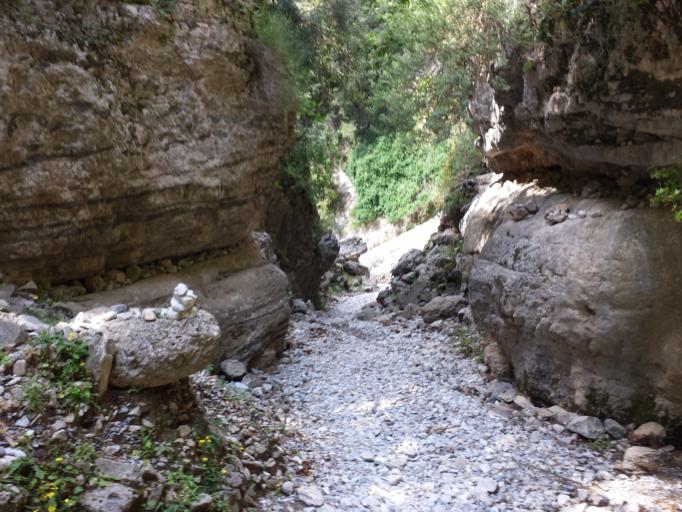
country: GR
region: Crete
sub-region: Nomos Chanias
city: Chora Sfakion
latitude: 35.2329
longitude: 24.1632
